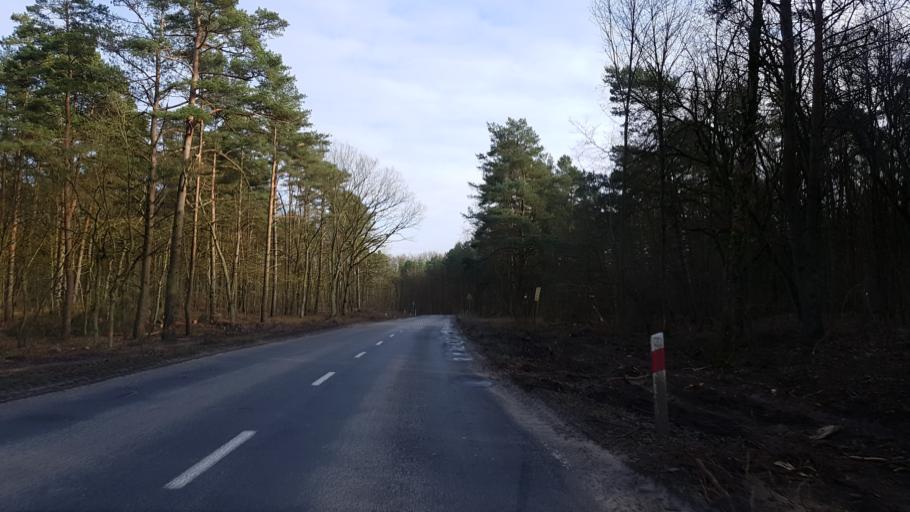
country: PL
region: West Pomeranian Voivodeship
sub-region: Powiat policki
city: Dobra
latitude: 53.4730
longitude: 14.4739
